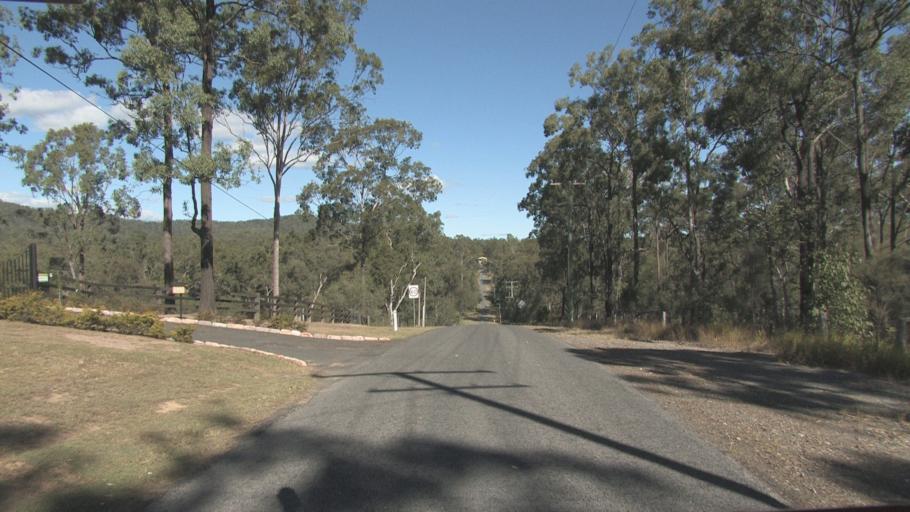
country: AU
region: Queensland
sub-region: Logan
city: Chambers Flat
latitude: -27.8154
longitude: 153.0775
